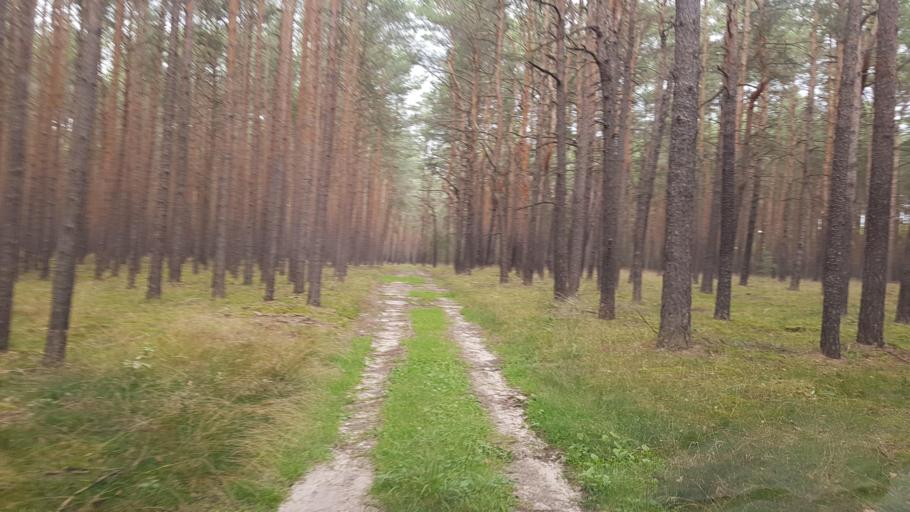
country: DE
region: Brandenburg
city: Crinitz
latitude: 51.7104
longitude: 13.7278
